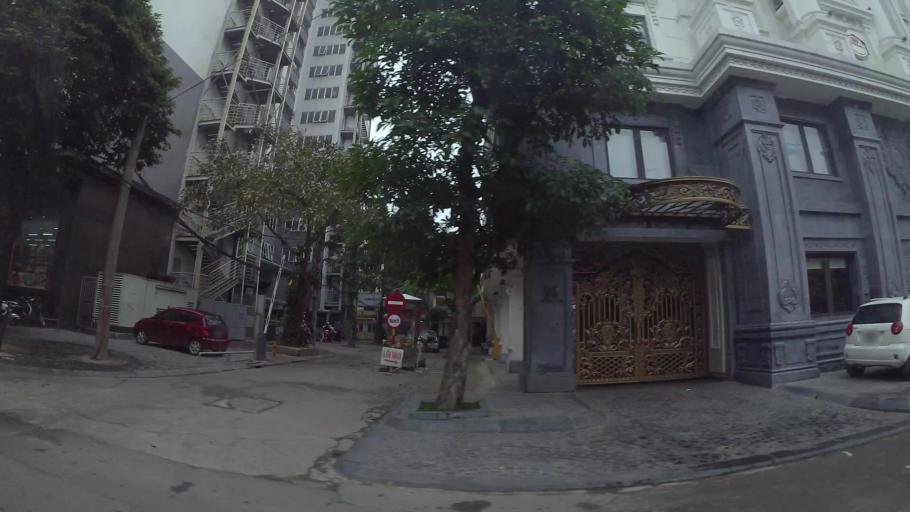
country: VN
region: Ha Noi
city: Dong Da
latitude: 21.0130
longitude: 105.8278
